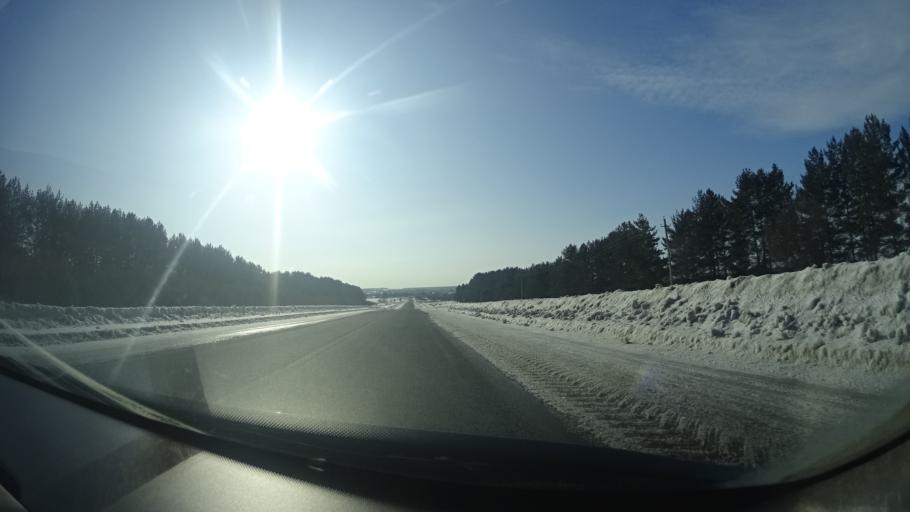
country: RU
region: Perm
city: Kuyeda
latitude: 56.4675
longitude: 55.5906
